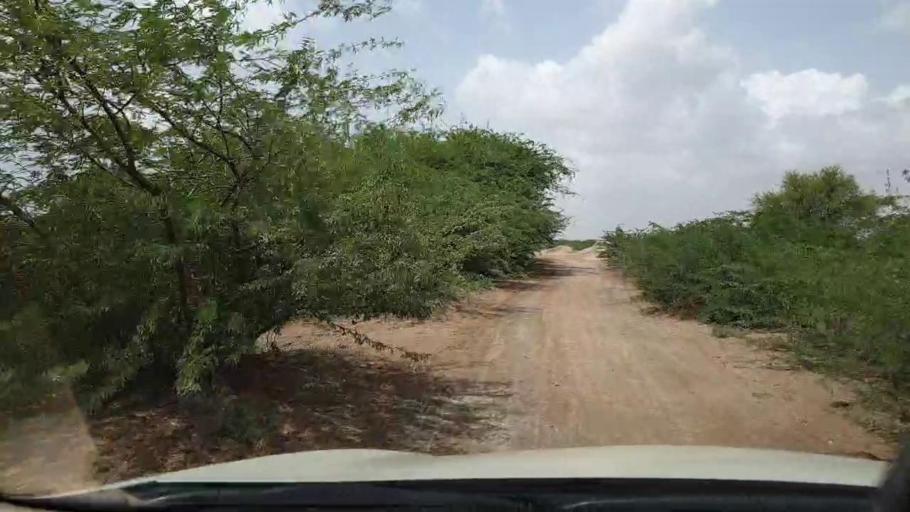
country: PK
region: Sindh
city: Kadhan
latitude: 24.3680
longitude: 68.8512
